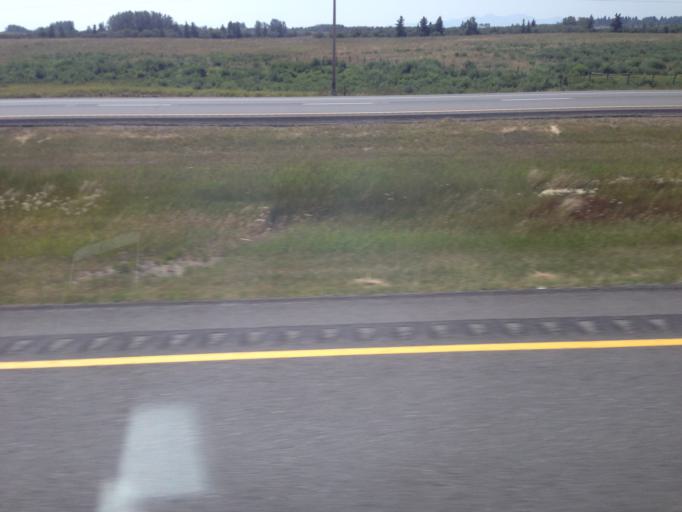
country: CA
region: Alberta
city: Cochrane
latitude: 51.1010
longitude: -114.6092
